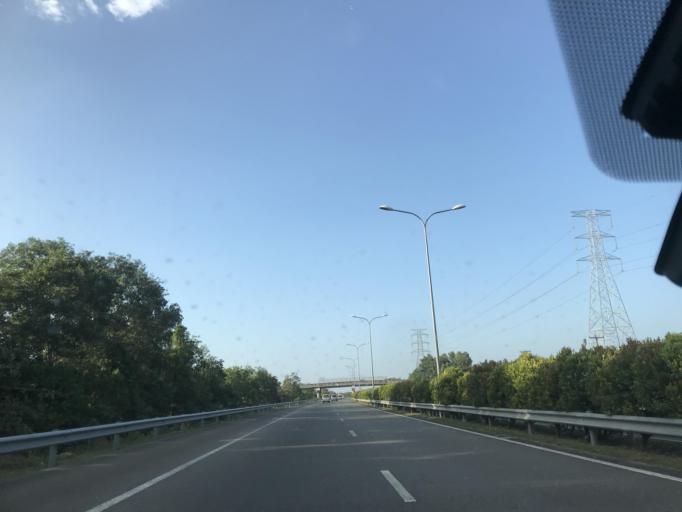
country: LK
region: Western
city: Kandana
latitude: 7.0472
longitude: 79.8821
